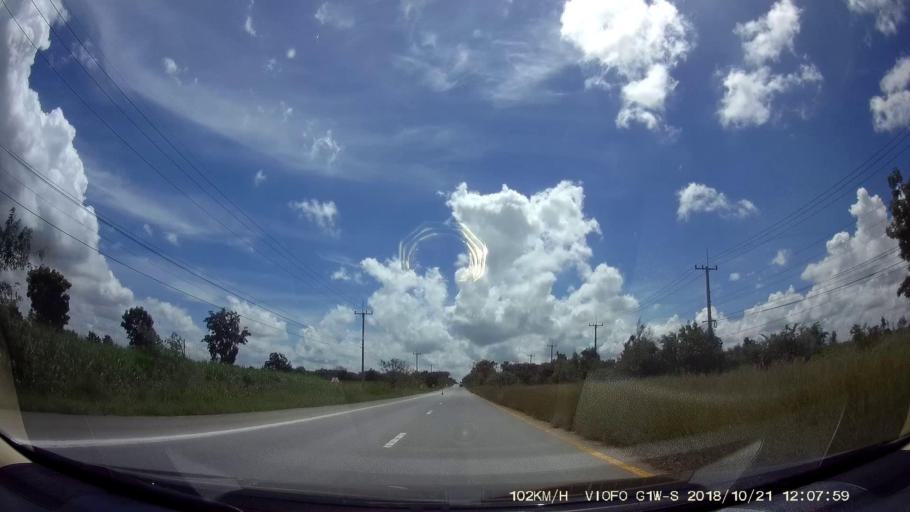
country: TH
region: Chaiyaphum
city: Chatturat
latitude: 15.4409
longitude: 101.8296
